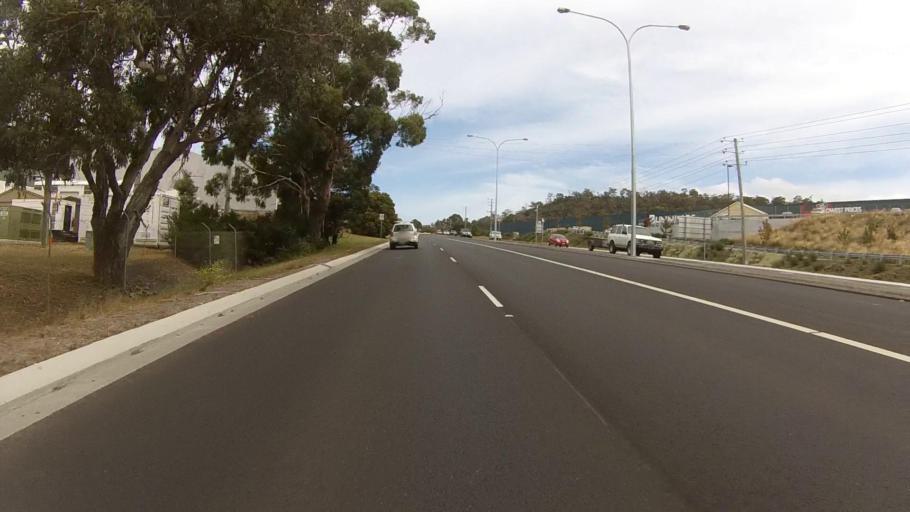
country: AU
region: Tasmania
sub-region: Clarence
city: Warrane
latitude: -42.8605
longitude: 147.3940
